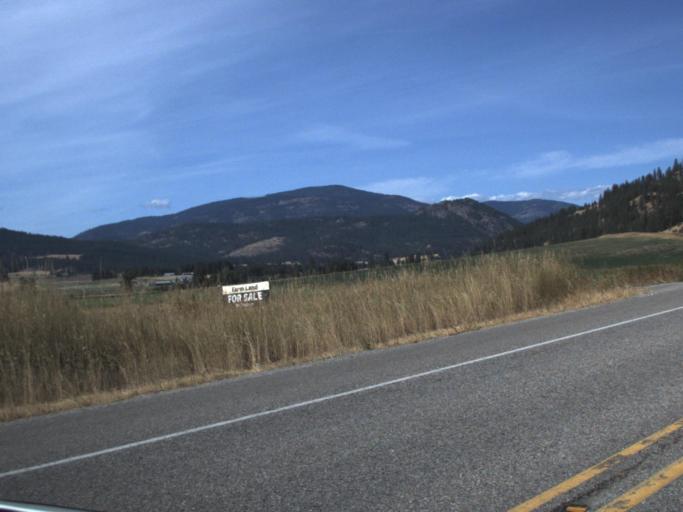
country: US
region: Washington
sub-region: Stevens County
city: Chewelah
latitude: 48.3049
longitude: -117.7767
